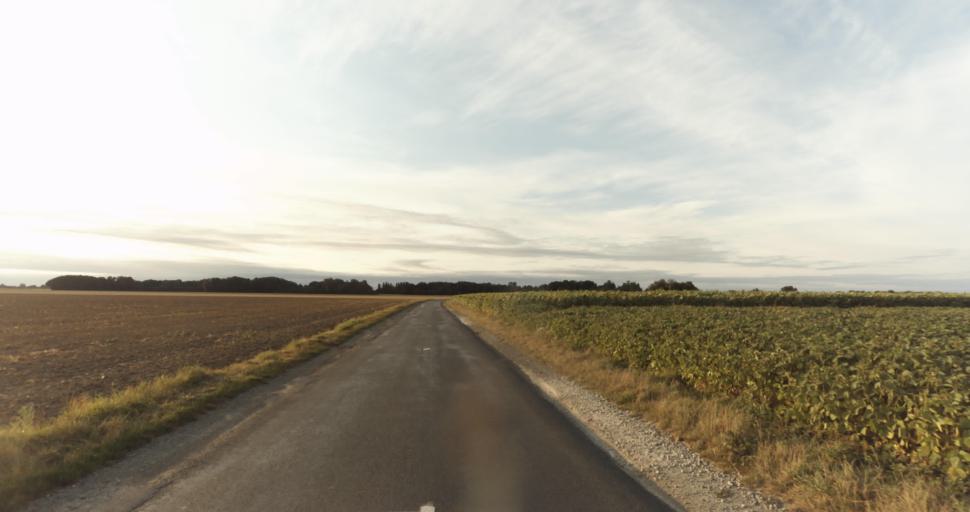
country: FR
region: Haute-Normandie
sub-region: Departement de l'Eure
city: Marcilly-sur-Eure
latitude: 48.8579
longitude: 1.2736
